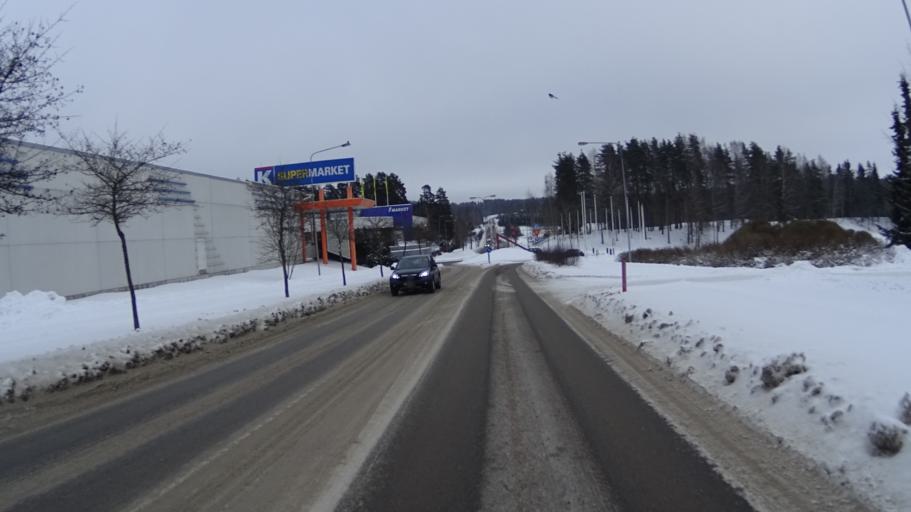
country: FI
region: Uusimaa
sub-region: Helsinki
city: Karkkila
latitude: 60.5340
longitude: 24.2295
